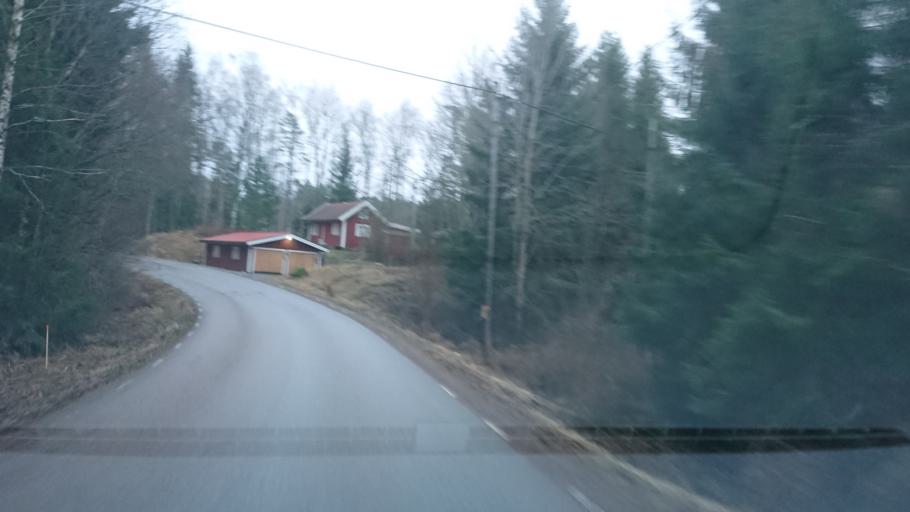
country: SE
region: Uppsala
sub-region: Osthammars Kommun
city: Bjorklinge
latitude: 60.0205
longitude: 17.5753
